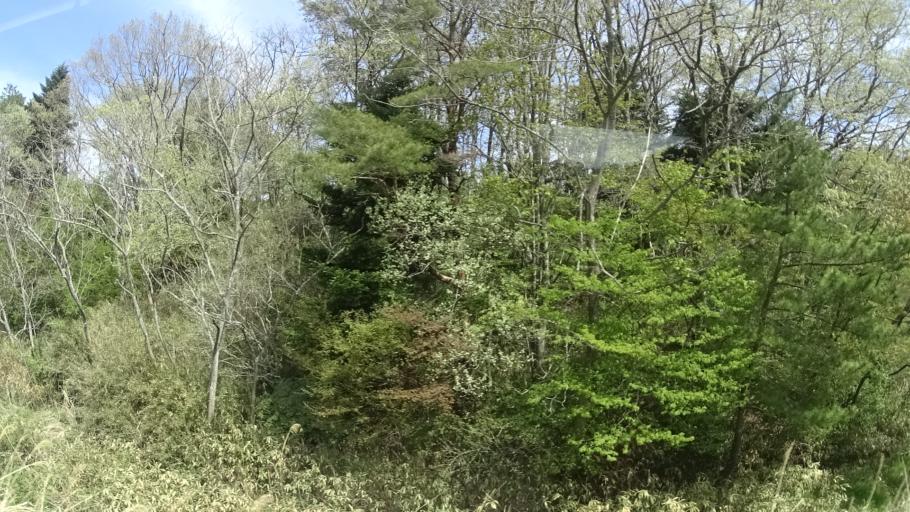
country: JP
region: Fukushima
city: Namie
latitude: 37.6193
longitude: 140.9880
